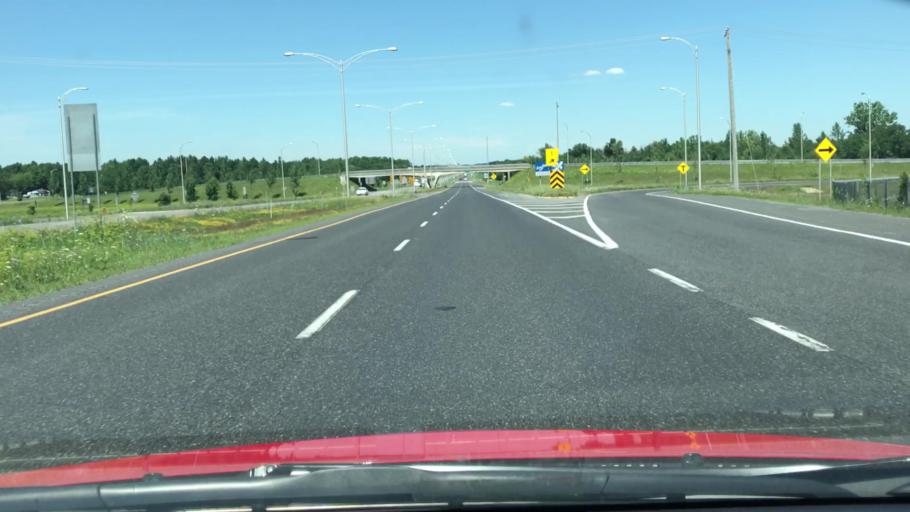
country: US
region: New York
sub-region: Clinton County
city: Champlain
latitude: 45.0174
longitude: -73.4527
